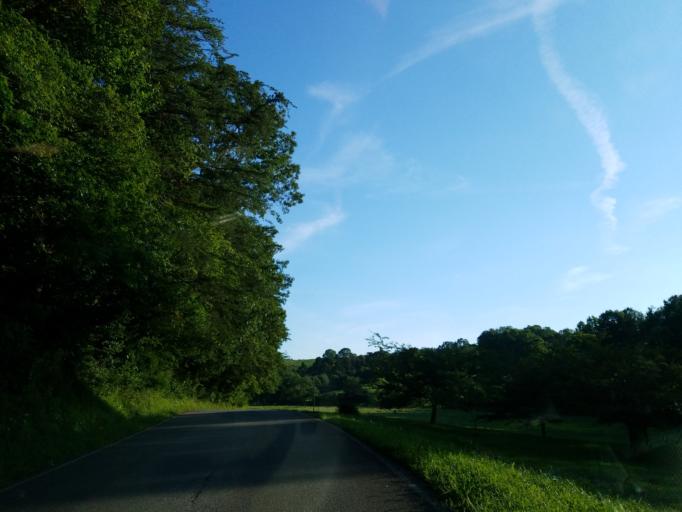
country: US
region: Georgia
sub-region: Pickens County
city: Jasper
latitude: 34.6065
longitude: -84.3228
